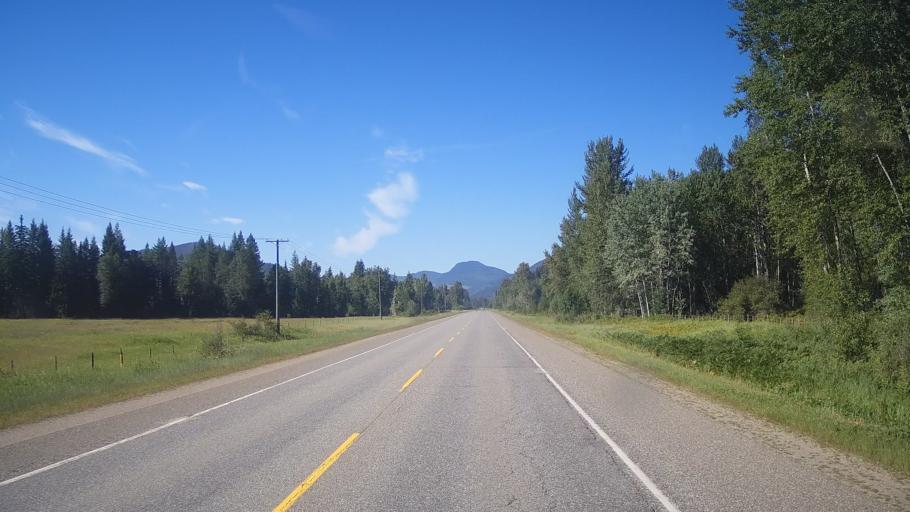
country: CA
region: British Columbia
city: Chase
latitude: 51.5946
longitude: -120.1227
